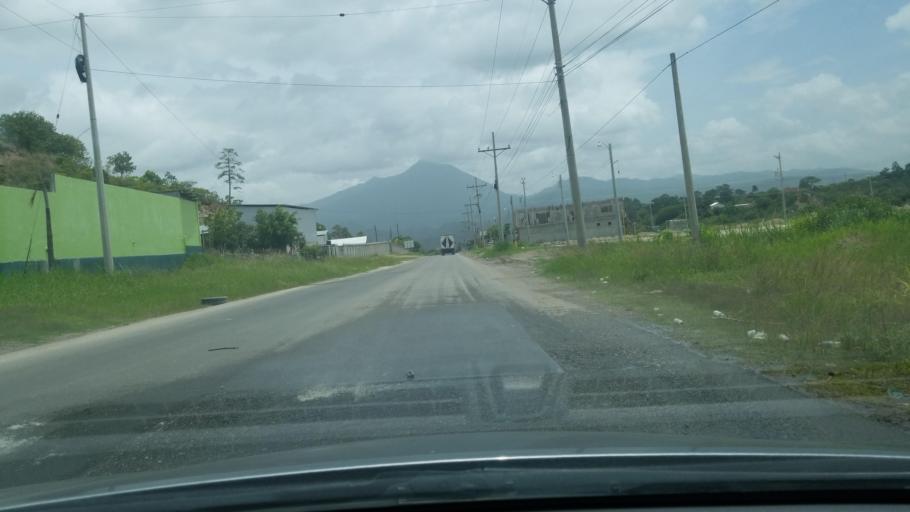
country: HN
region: Copan
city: Cucuyagua
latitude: 14.6692
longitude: -88.8581
